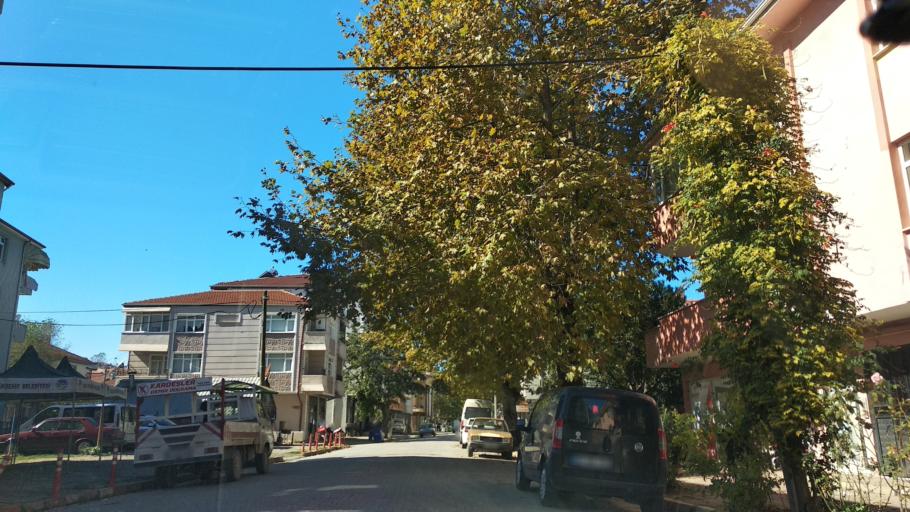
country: TR
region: Sakarya
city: Karasu
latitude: 41.0919
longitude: 30.6966
